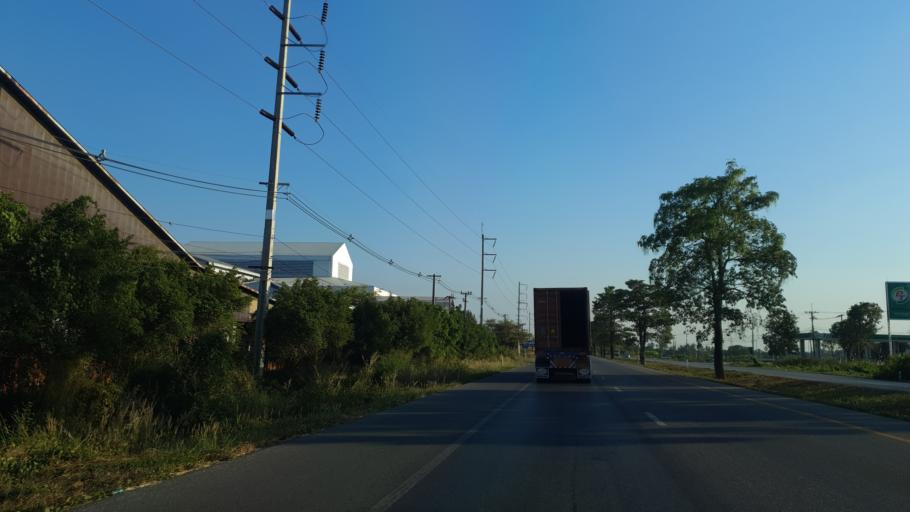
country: TH
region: Kamphaeng Phet
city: Khlong Khlung
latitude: 16.2523
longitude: 99.6897
